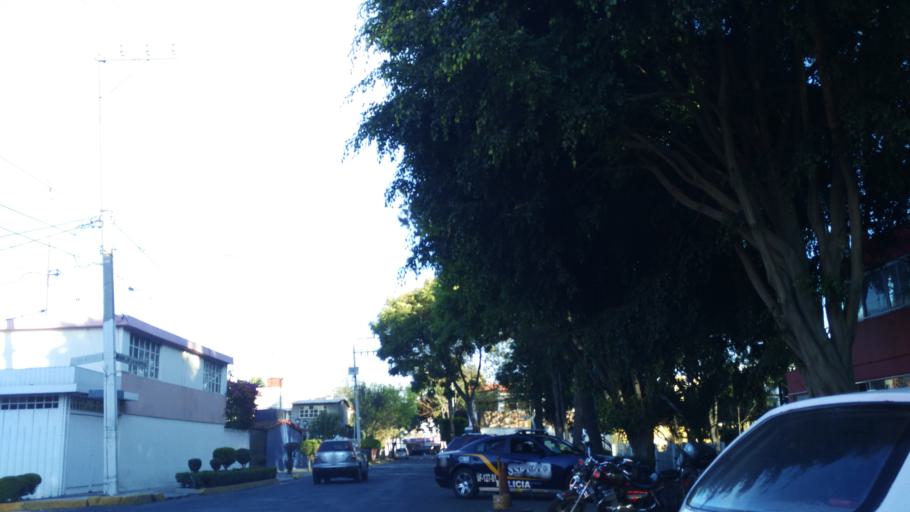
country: MX
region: Mexico City
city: Xochimilco
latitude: 19.2933
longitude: -99.1118
